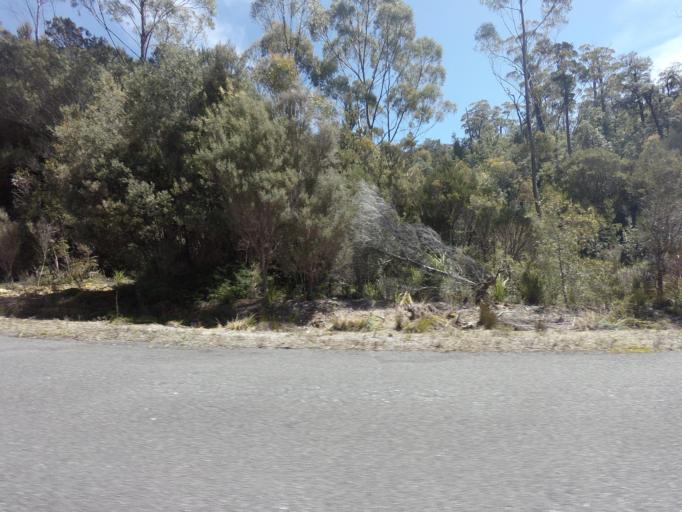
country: AU
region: Tasmania
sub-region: West Coast
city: Queenstown
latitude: -42.7789
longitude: 146.0361
